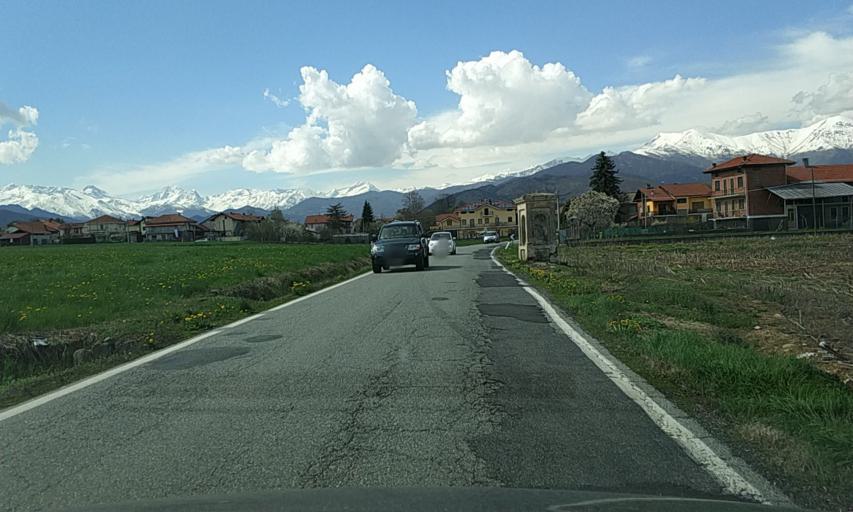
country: IT
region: Piedmont
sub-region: Provincia di Torino
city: Nole
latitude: 45.2556
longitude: 7.5854
